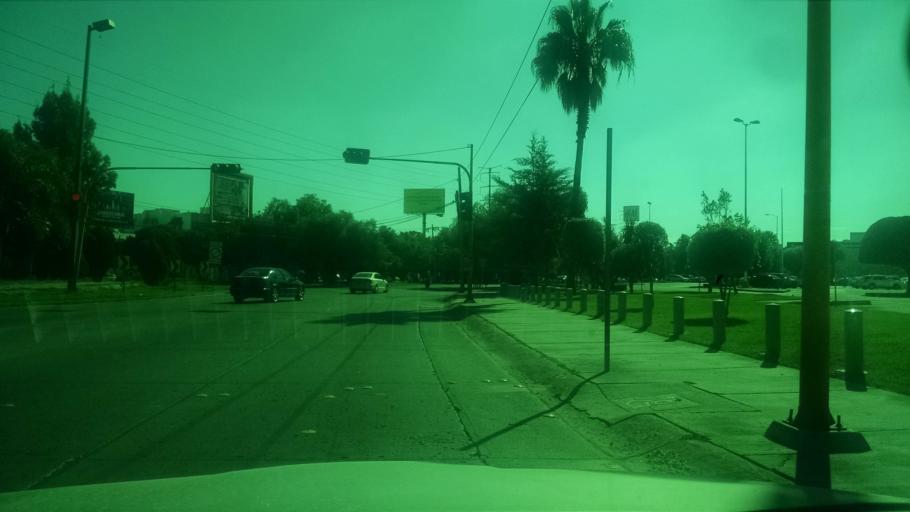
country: MX
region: Guanajuato
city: Leon
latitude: 21.1576
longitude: -101.6921
